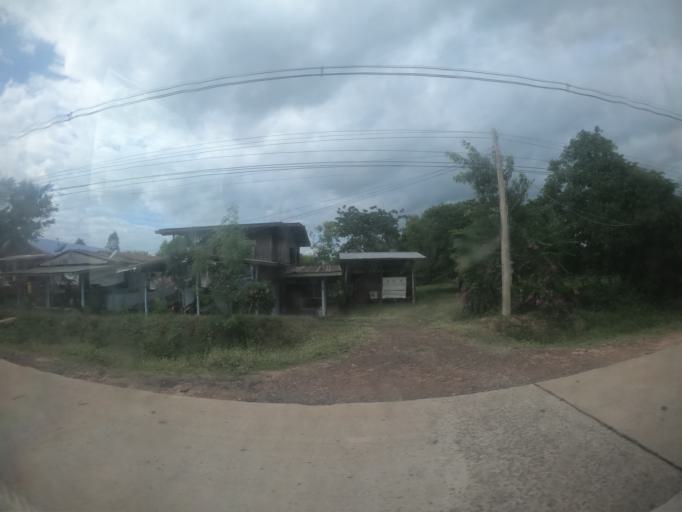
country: TH
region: Surin
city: Kap Choeng
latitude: 14.5473
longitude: 103.5132
